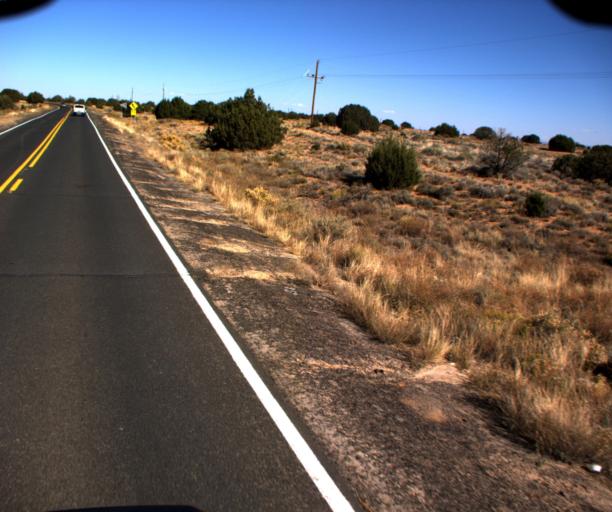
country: US
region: Arizona
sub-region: Navajo County
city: First Mesa
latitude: 35.8350
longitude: -110.5283
